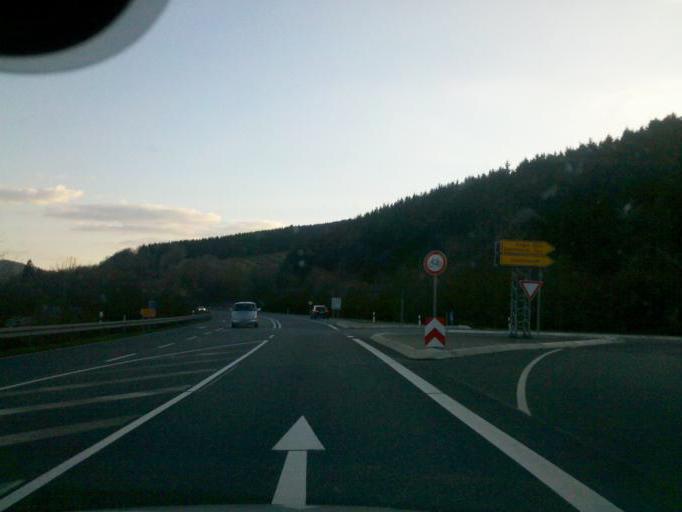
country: DE
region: Hesse
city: Dillenburg
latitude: 50.8067
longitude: 8.3381
